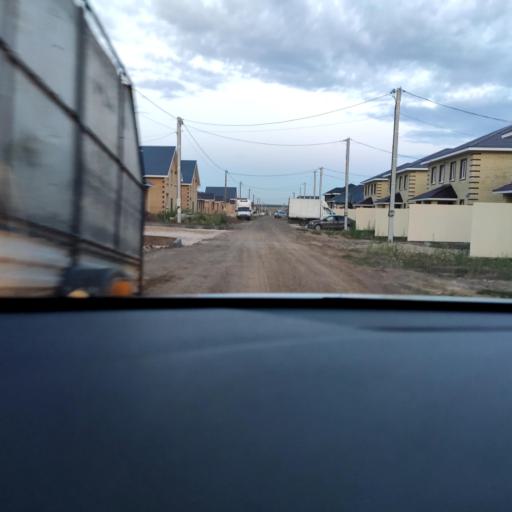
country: RU
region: Tatarstan
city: Stolbishchi
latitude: 55.7173
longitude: 49.2971
